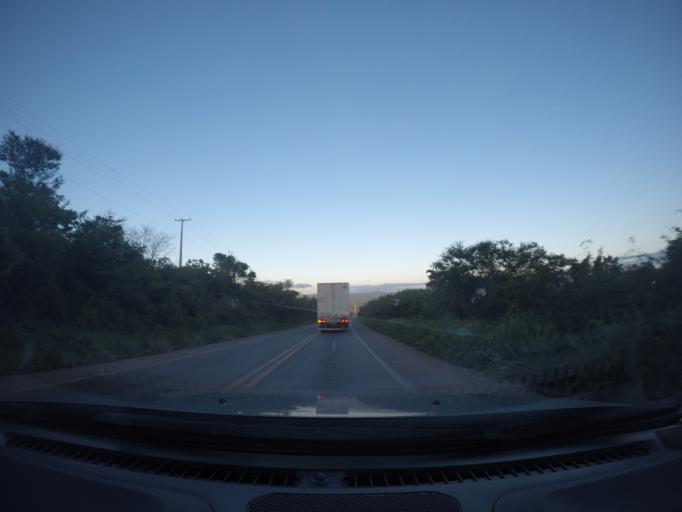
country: BR
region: Bahia
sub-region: Seabra
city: Seabra
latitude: -12.4137
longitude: -41.9779
